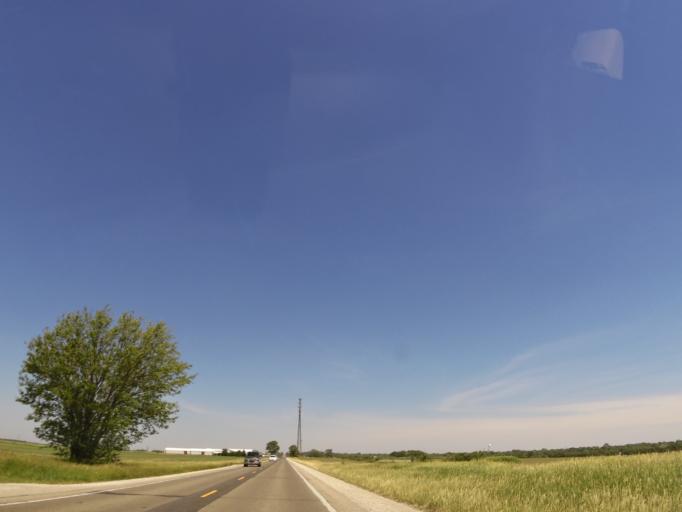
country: US
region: Illinois
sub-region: Vermilion County
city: Hoopeston
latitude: 40.4456
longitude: -87.6866
